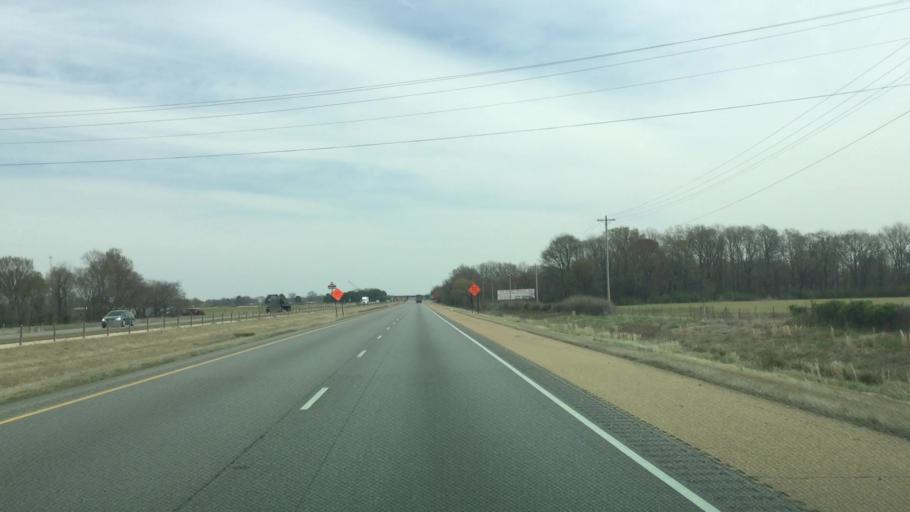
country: US
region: Arkansas
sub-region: Saint Francis County
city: Forrest City
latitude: 34.9785
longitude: -90.9170
